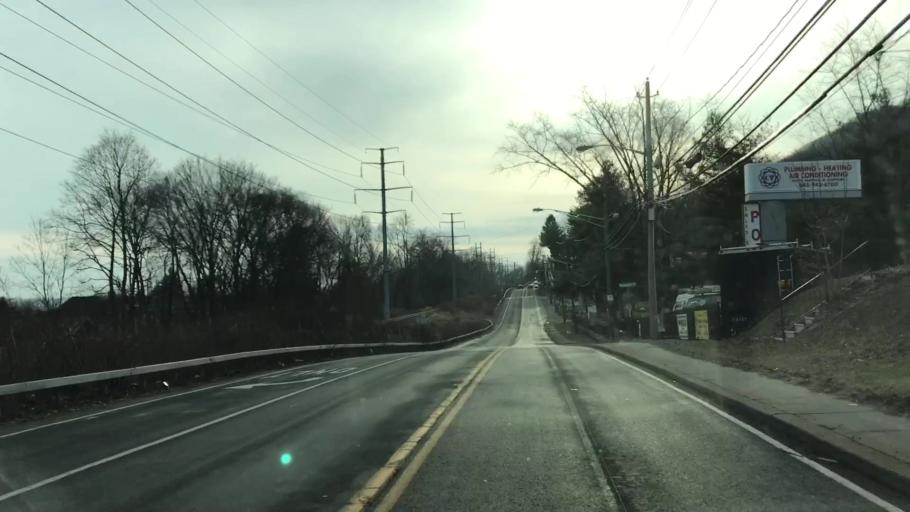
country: US
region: New York
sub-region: Rockland County
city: Haverstraw
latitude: 41.1940
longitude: -73.9683
